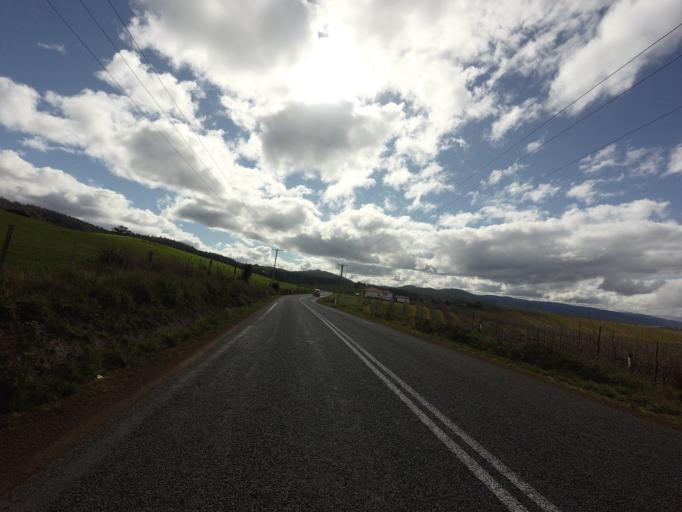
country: AU
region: Tasmania
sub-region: Huon Valley
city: Geeveston
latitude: -43.2086
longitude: 146.9752
